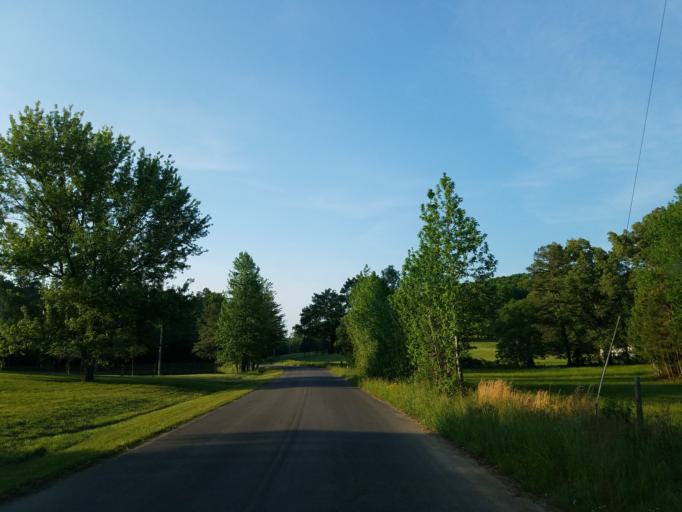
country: US
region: Georgia
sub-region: Whitfield County
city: Dalton
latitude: 34.6611
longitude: -85.0801
